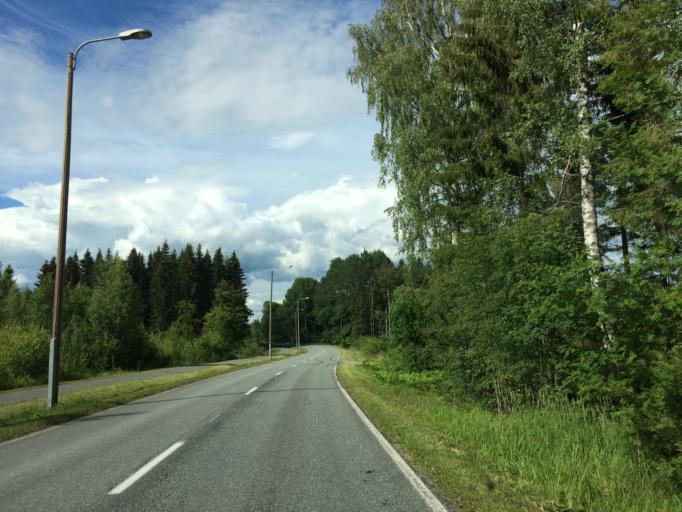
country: FI
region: Haeme
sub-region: Haemeenlinna
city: Janakkala
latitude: 60.9150
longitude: 24.6122
